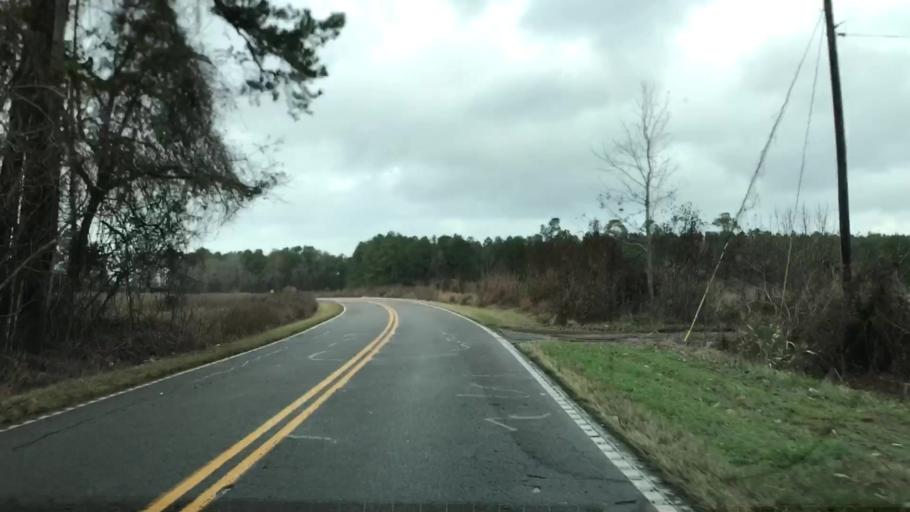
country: US
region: South Carolina
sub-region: Florence County
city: Johnsonville
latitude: 33.6580
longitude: -79.3043
